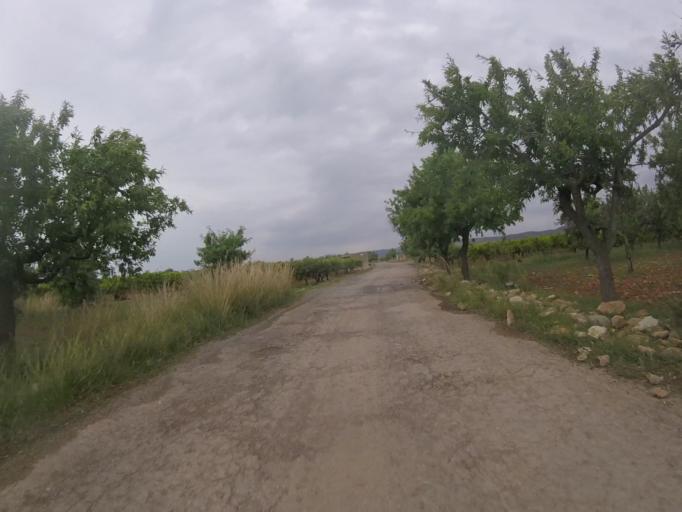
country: ES
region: Valencia
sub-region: Provincia de Castello
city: Torreblanca
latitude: 40.2209
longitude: 0.2119
